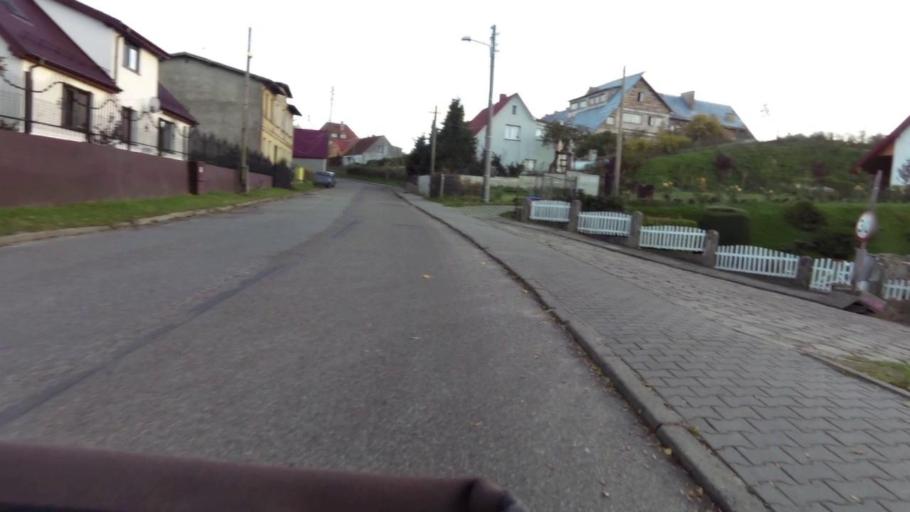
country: PL
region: West Pomeranian Voivodeship
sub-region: Powiat kamienski
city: Miedzyzdroje
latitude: 53.8694
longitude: 14.4280
